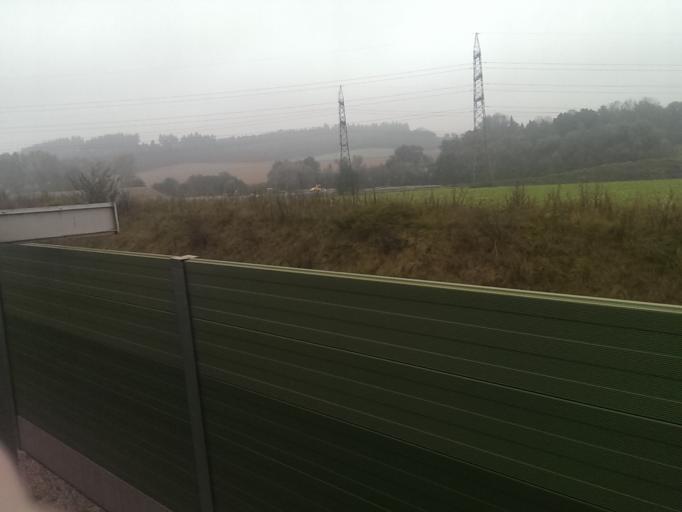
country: AT
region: Upper Austria
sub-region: Wels-Land
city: Stadl-Paura
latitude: 48.0951
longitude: 13.8559
